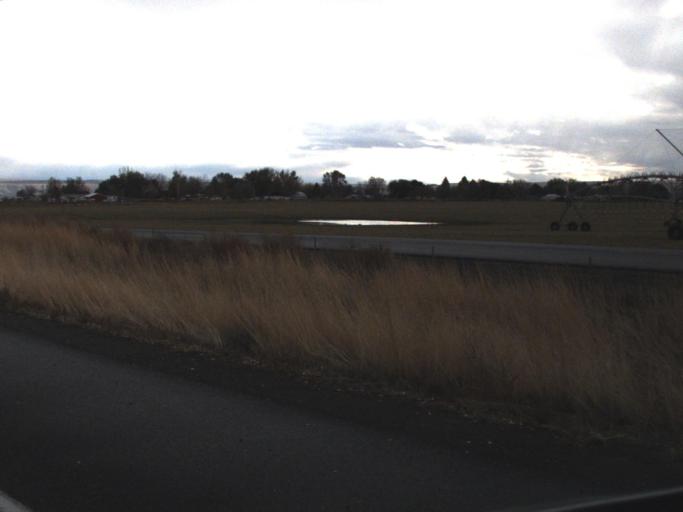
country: US
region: Washington
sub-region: Walla Walla County
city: Burbank
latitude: 46.1869
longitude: -118.9811
